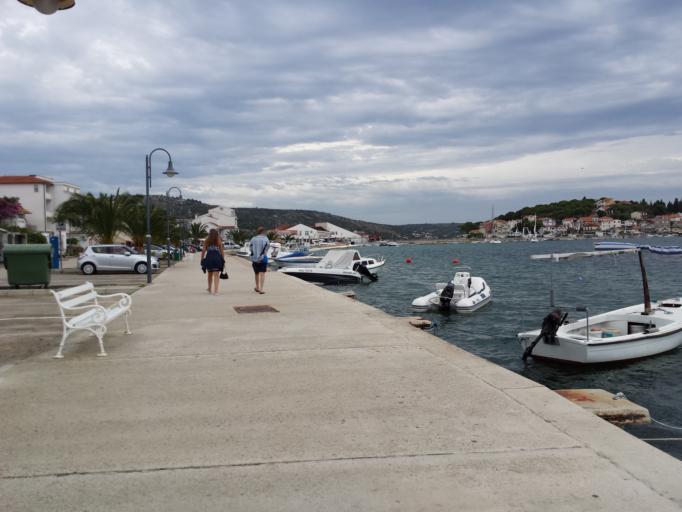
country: HR
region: Sibensko-Kniniska
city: Rogoznica
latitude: 43.5331
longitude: 15.9650
